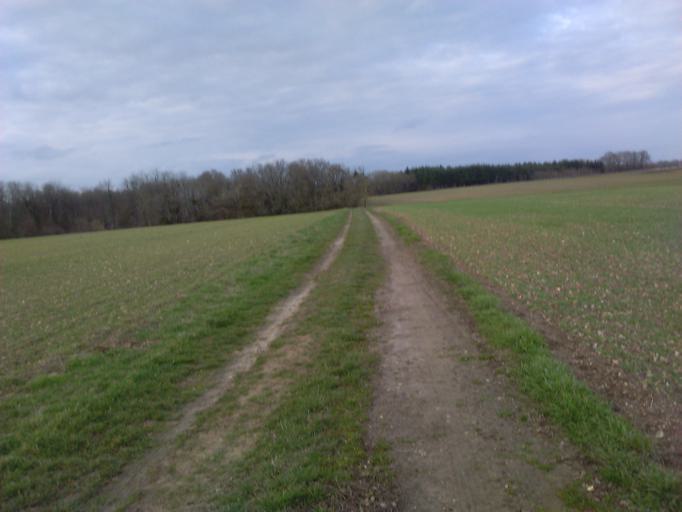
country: FR
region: Centre
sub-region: Departement du Loir-et-Cher
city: Villiers-sur-Loir
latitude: 47.8172
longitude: 0.9773
